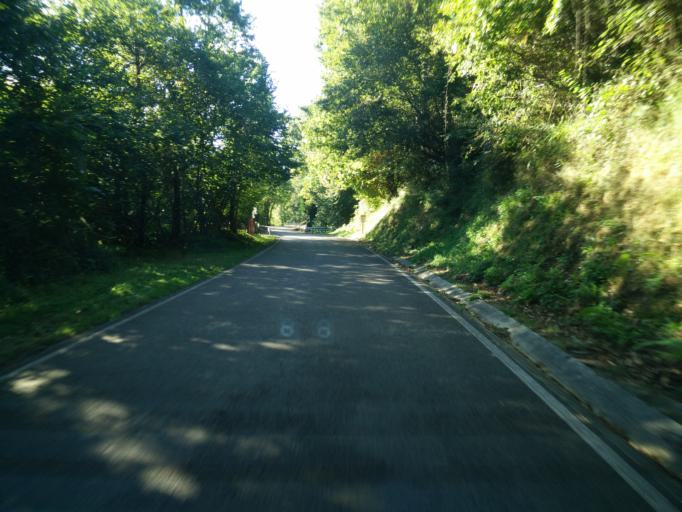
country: ES
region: Cantabria
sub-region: Provincia de Cantabria
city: San Pedro del Romeral
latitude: 43.1525
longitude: -3.8212
